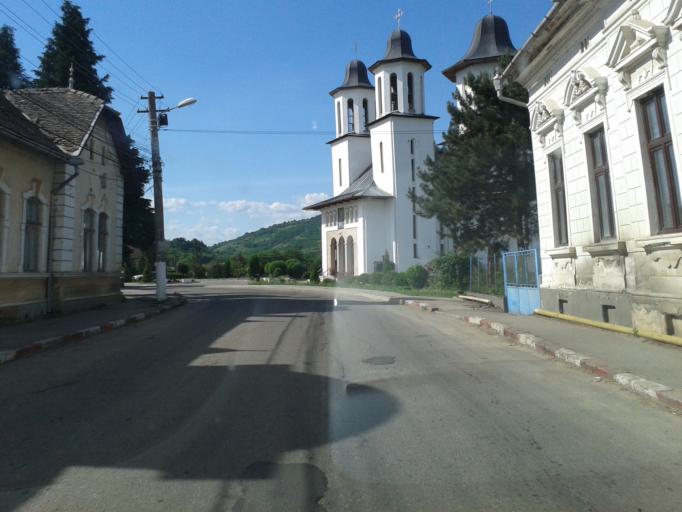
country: RO
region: Hunedoara
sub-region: Comuna Geoagiu
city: Geoagiu
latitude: 45.9244
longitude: 23.1993
